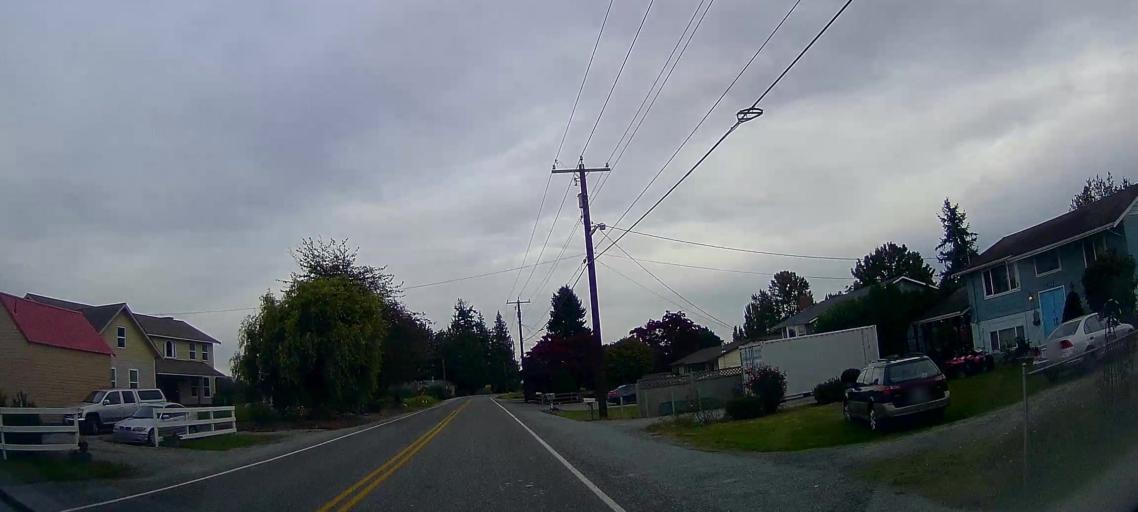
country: US
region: Washington
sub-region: Skagit County
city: Mount Vernon
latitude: 48.4554
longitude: -122.3796
